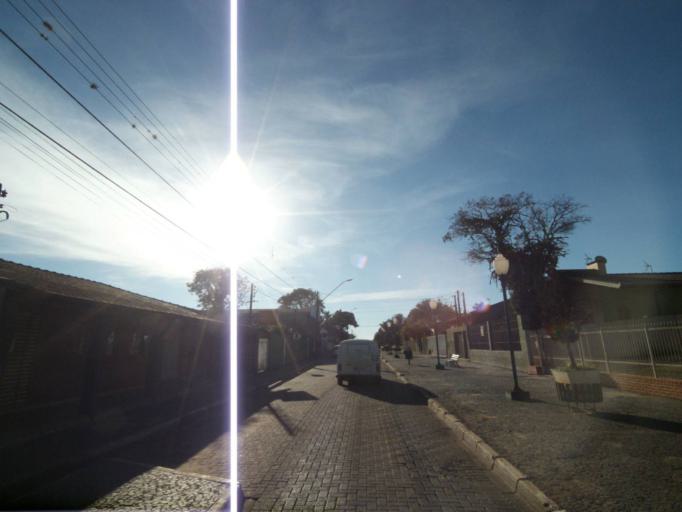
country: BR
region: Parana
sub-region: Tibagi
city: Tibagi
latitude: -24.5170
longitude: -50.4094
